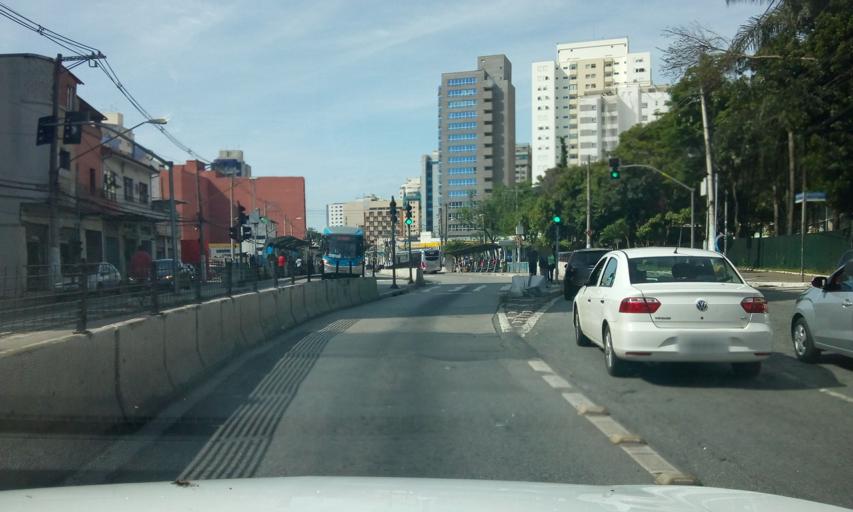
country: BR
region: Sao Paulo
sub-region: Sao Paulo
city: Sao Paulo
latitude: -23.6053
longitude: -46.6753
